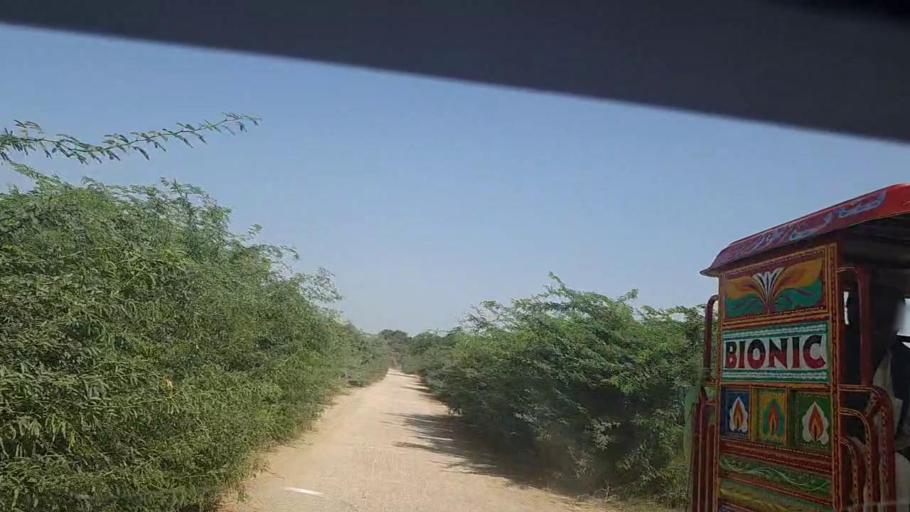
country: PK
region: Sindh
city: Rajo Khanani
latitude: 24.9698
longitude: 68.8729
